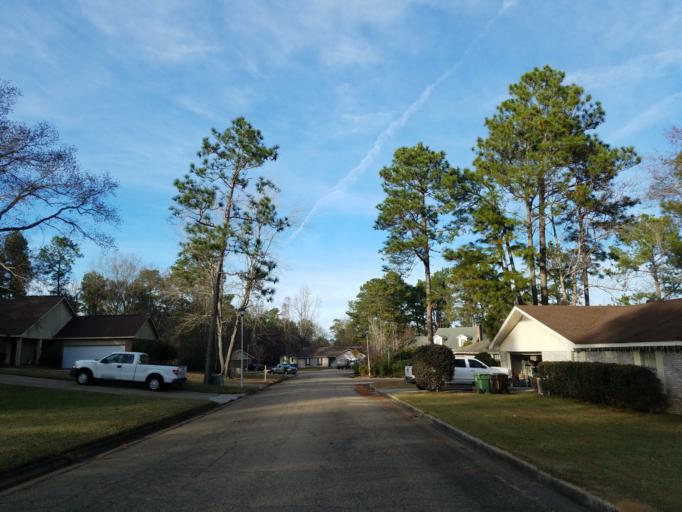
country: US
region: Mississippi
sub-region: Lamar County
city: West Hattiesburg
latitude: 31.3126
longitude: -89.3515
